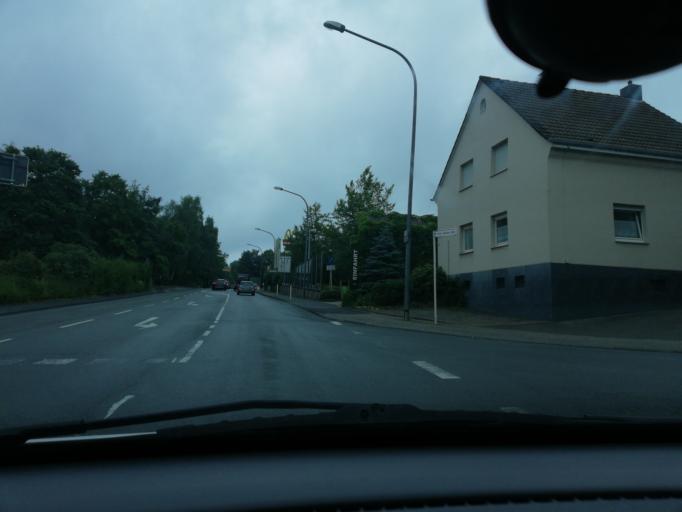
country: DE
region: North Rhine-Westphalia
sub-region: Regierungsbezirk Dusseldorf
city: Wuppertal
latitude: 51.2340
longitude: 7.2125
